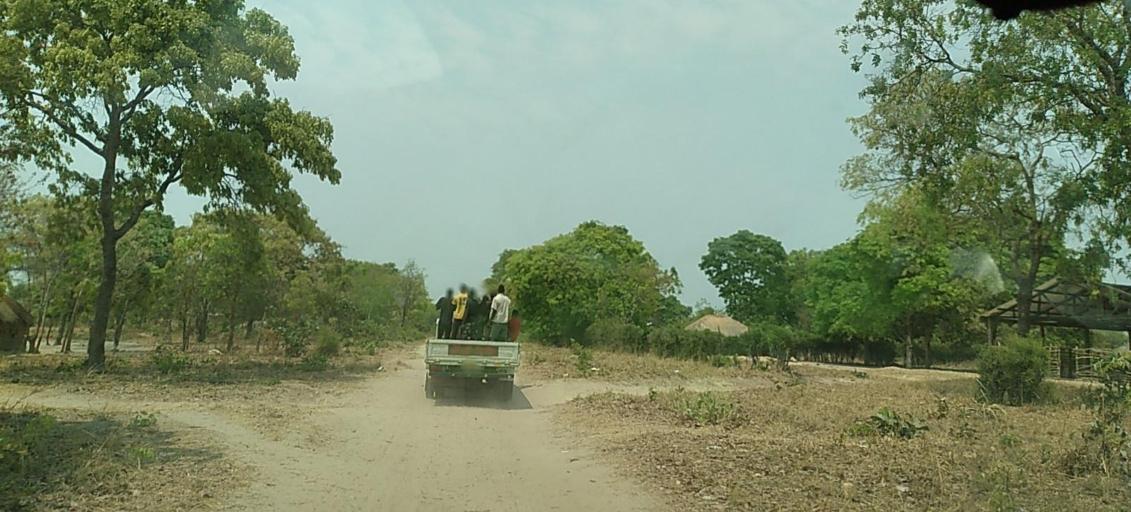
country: ZM
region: North-Western
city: Kabompo
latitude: -13.4859
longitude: 24.4614
